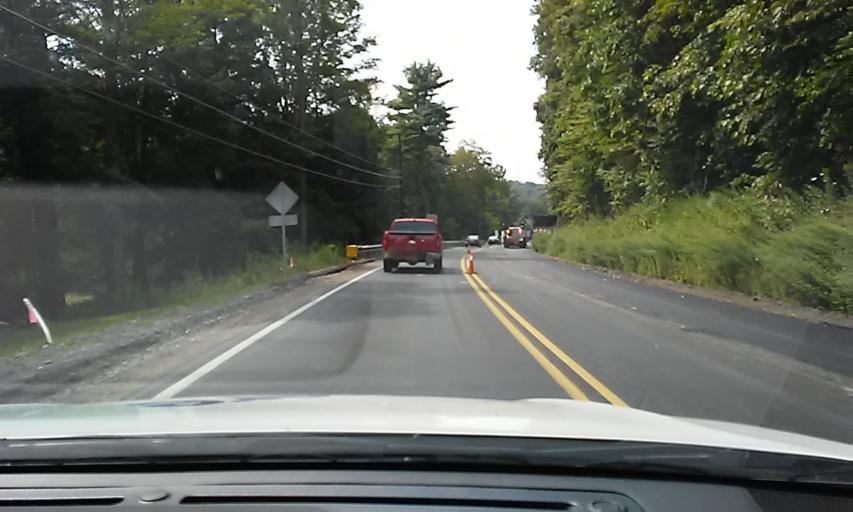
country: US
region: Pennsylvania
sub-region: Clearfield County
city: Treasure Lake
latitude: 41.1843
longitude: -78.6071
